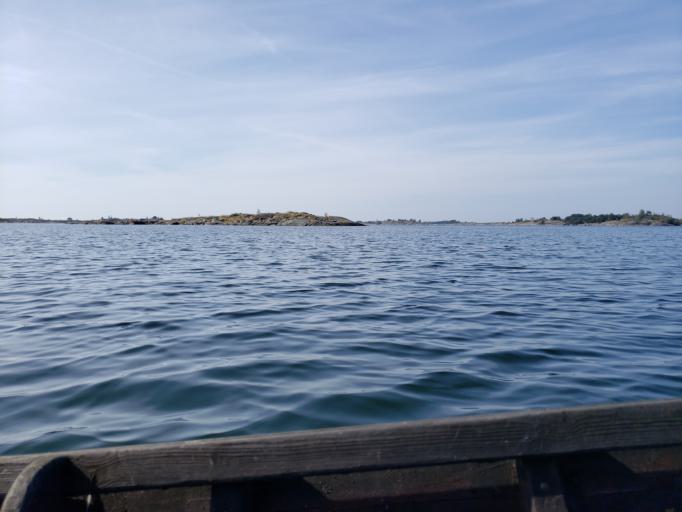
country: FI
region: Varsinais-Suomi
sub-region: Aboland-Turunmaa
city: Dragsfjaerd
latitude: 59.8523
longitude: 22.2195
